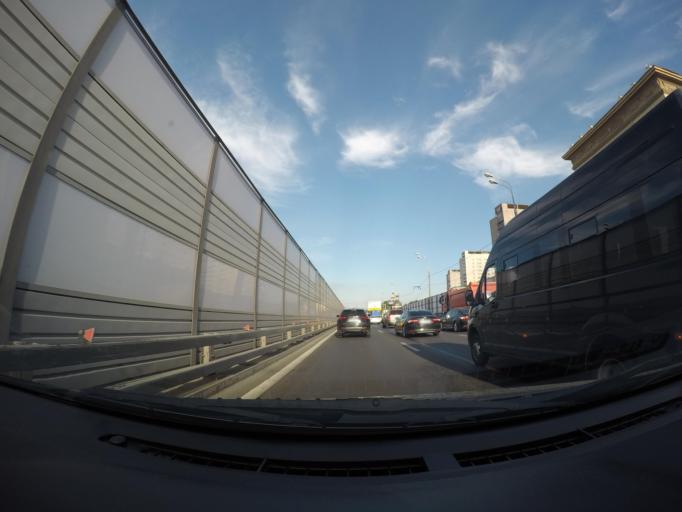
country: RU
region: Moscow
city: Mar'ina Roshcha
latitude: 55.7893
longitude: 37.6335
